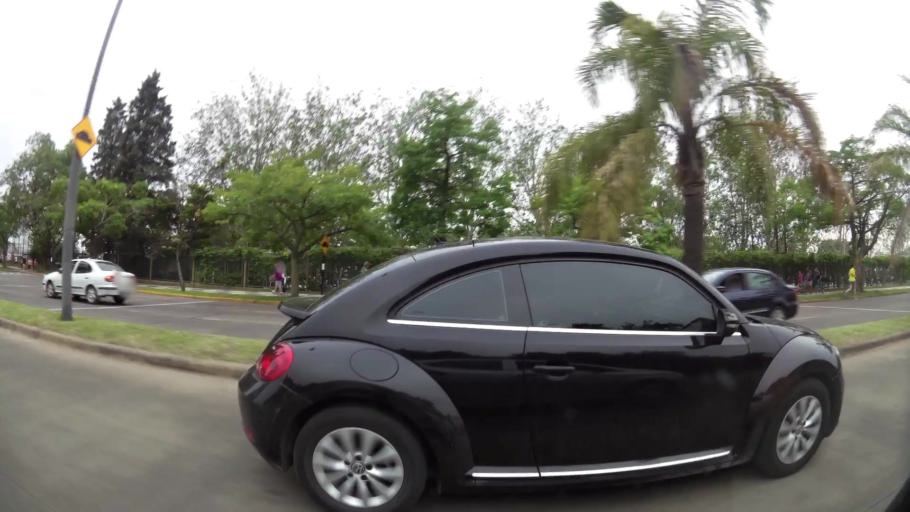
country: AR
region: Santa Fe
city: Granadero Baigorria
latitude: -32.9003
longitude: -60.6828
